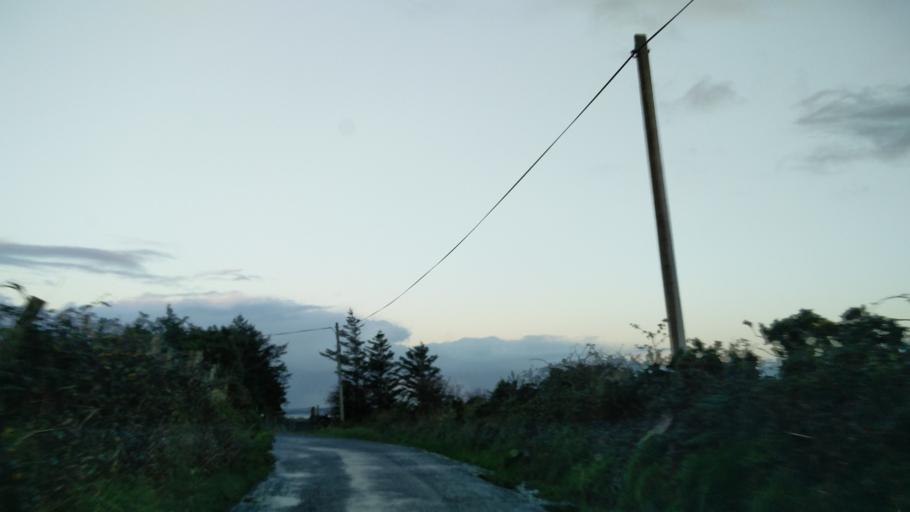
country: IE
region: Connaught
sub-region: Maigh Eo
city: Westport
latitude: 53.7824
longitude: -9.6685
